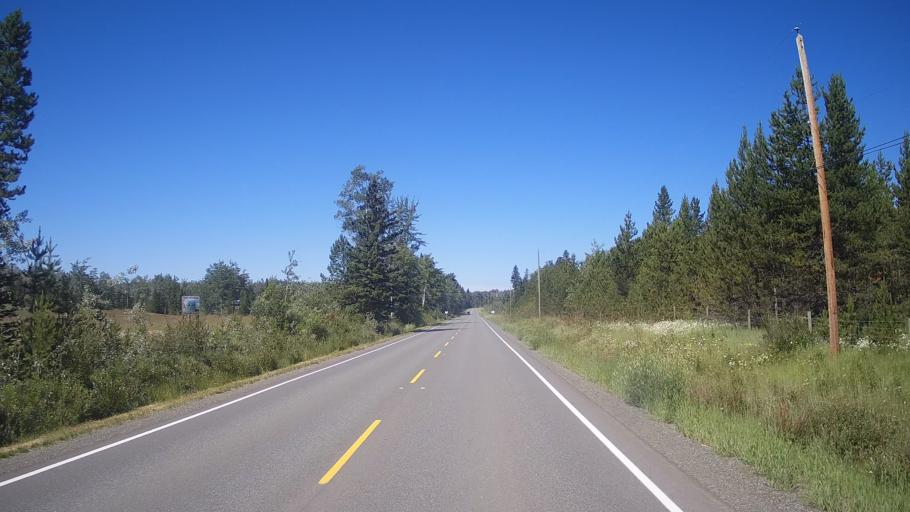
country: CA
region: British Columbia
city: Cache Creek
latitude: 51.5402
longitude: -121.0376
